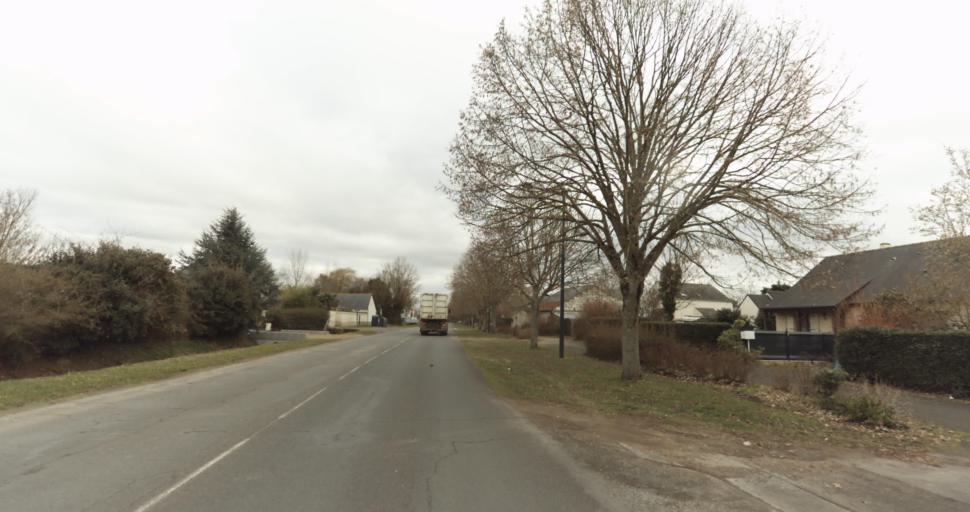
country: FR
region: Pays de la Loire
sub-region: Departement de Maine-et-Loire
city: Saumur
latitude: 47.2752
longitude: -0.0725
